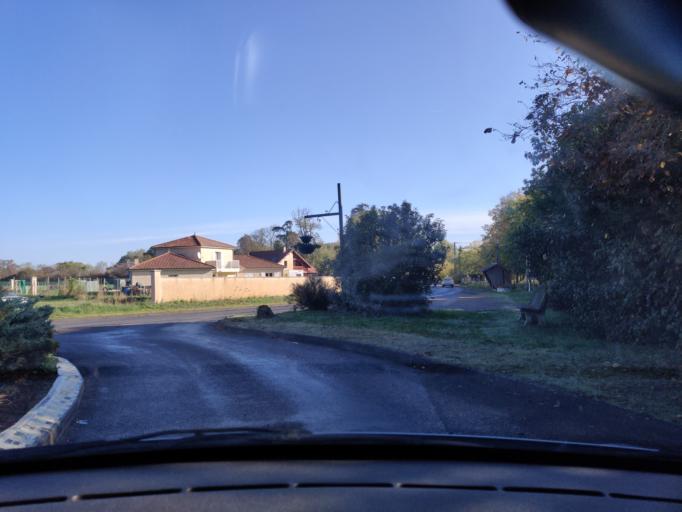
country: FR
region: Auvergne
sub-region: Departement du Puy-de-Dome
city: Combronde
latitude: 46.0408
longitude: 3.1295
